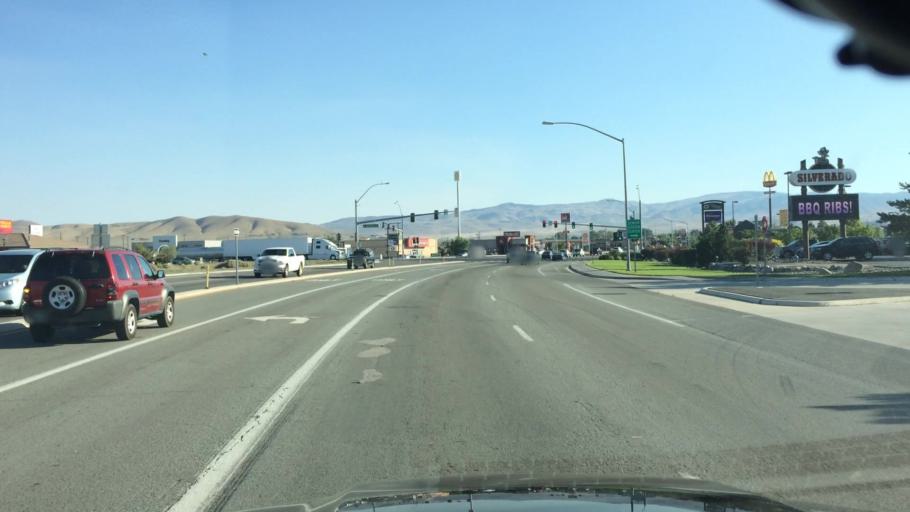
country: US
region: Nevada
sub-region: Lyon County
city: Fernley
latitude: 39.6107
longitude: -119.2192
